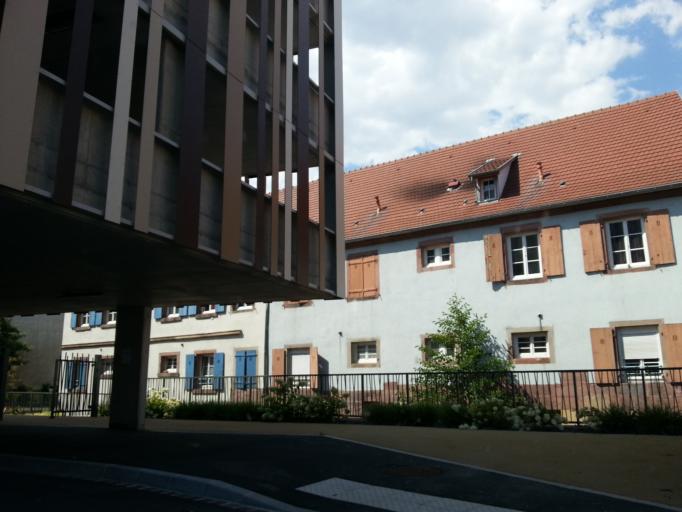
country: FR
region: Alsace
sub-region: Departement du Haut-Rhin
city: Colmar
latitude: 48.0757
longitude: 7.3652
